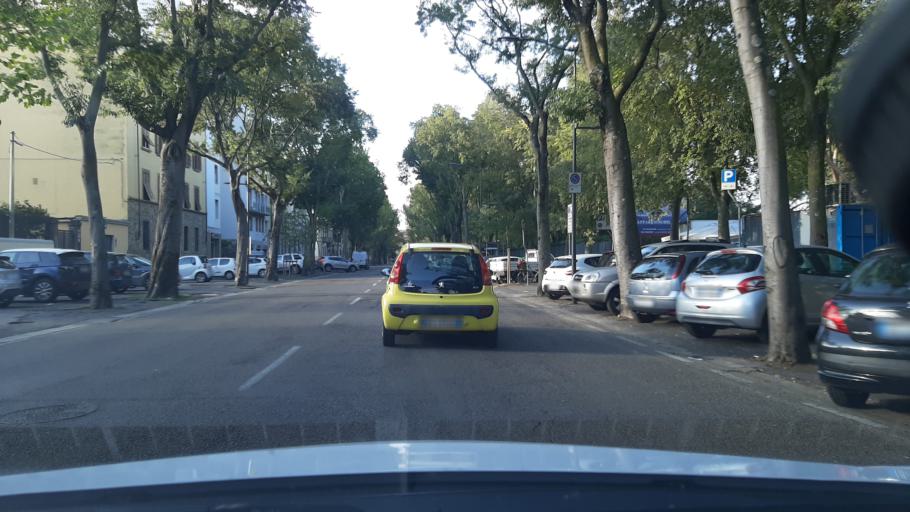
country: IT
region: Tuscany
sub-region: Province of Florence
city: Fiesole
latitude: 43.7769
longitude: 11.2863
